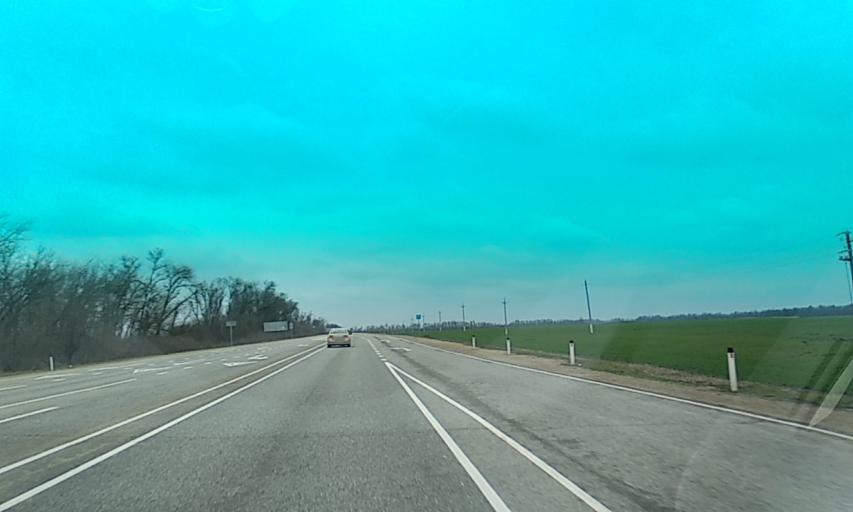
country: RU
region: Adygeya
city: Krasnogvardeyskoye
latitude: 45.1291
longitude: 39.6348
